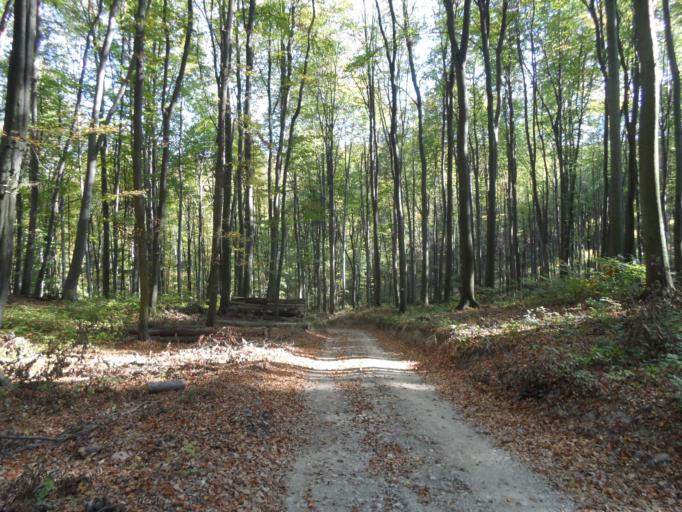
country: HU
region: Veszprem
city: Urkut
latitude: 47.2080
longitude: 17.6266
